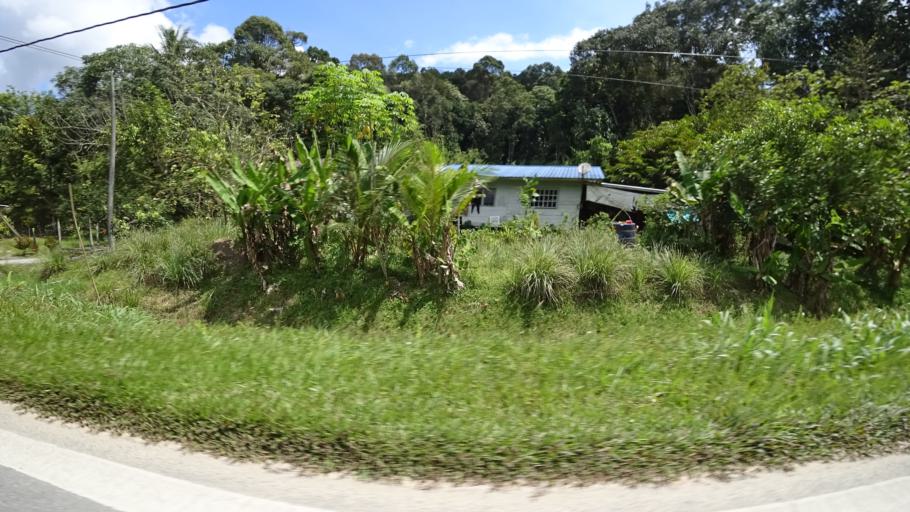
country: MY
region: Sarawak
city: Limbang
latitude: 4.6771
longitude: 114.9817
